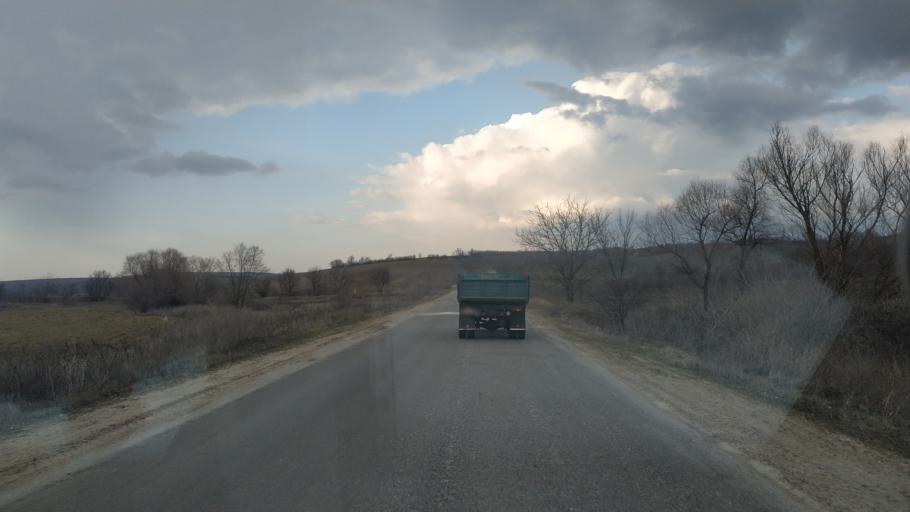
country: MD
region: Anenii Noi
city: Anenii Noi
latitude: 46.9471
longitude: 29.2828
